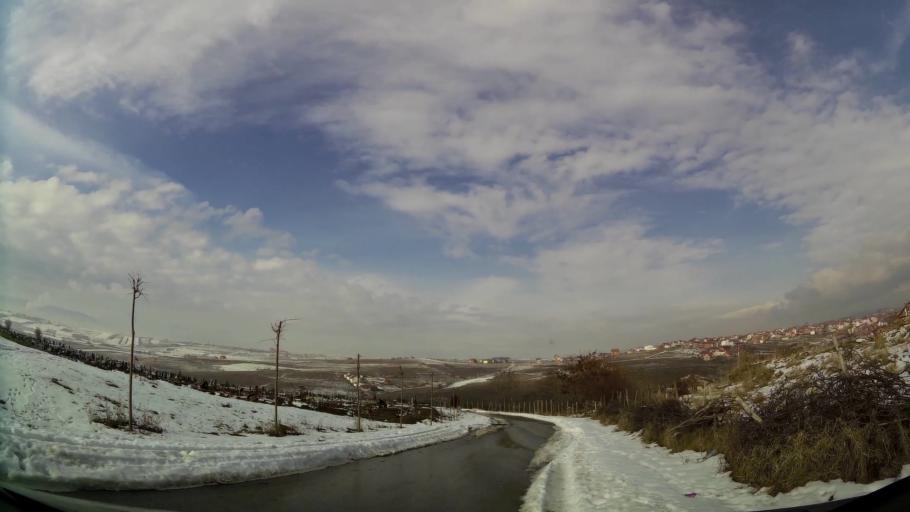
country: XK
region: Pristina
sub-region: Komuna e Prishtines
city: Pristina
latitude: 42.6753
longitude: 21.1514
